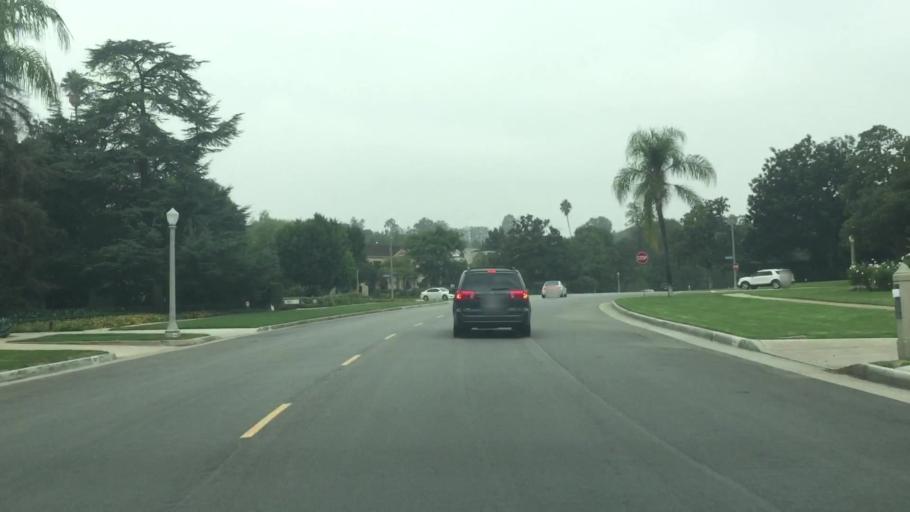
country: US
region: California
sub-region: Los Angeles County
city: San Marino
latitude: 34.1173
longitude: -118.1229
